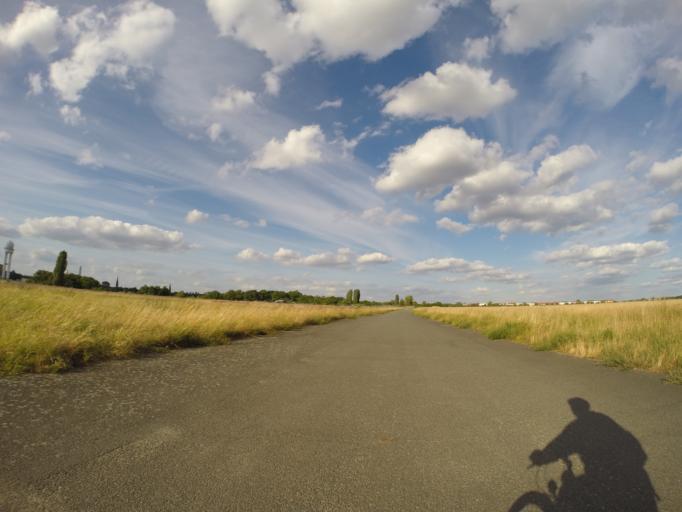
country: DE
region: Berlin
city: Tempelhof Bezirk
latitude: 52.4762
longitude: 13.3997
